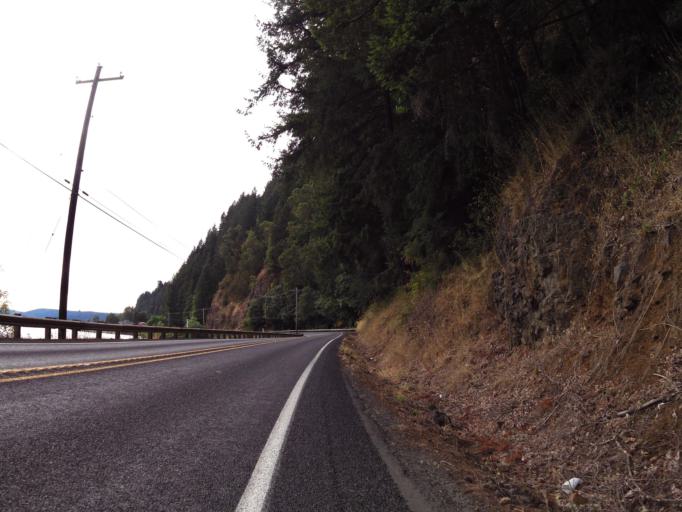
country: US
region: Washington
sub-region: Cowlitz County
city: West Longview
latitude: 46.1904
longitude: -123.1137
